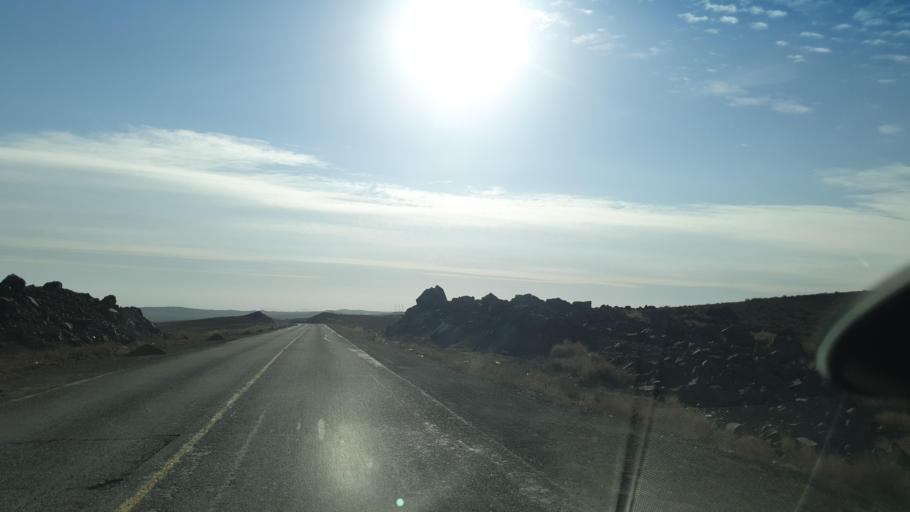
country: KZ
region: Zhambyl
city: Mynaral
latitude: 45.7075
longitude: 73.3991
